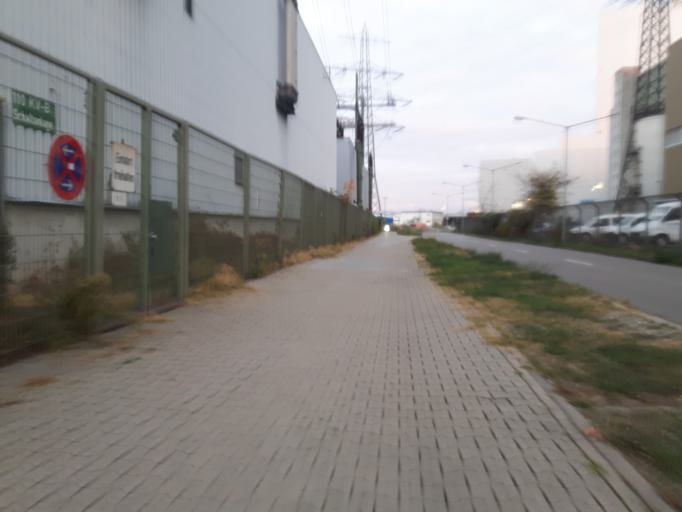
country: DE
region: Rheinland-Pfalz
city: Altrip
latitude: 49.4450
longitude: 8.5011
